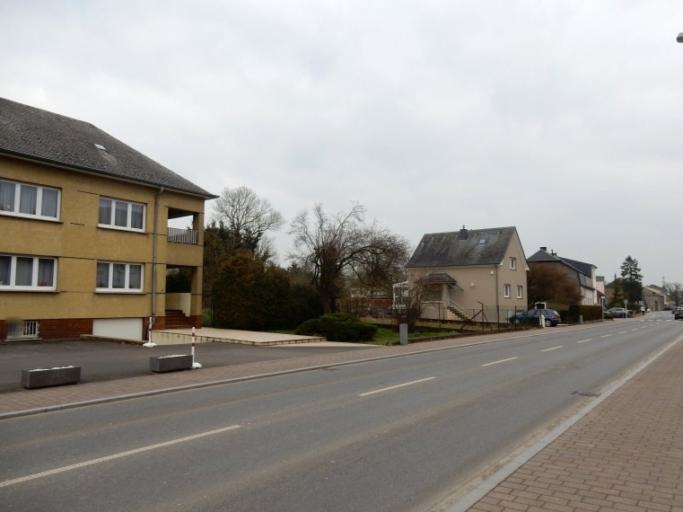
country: LU
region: Luxembourg
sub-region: Canton d'Esch-sur-Alzette
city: Mondercange
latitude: 49.5321
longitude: 5.9888
